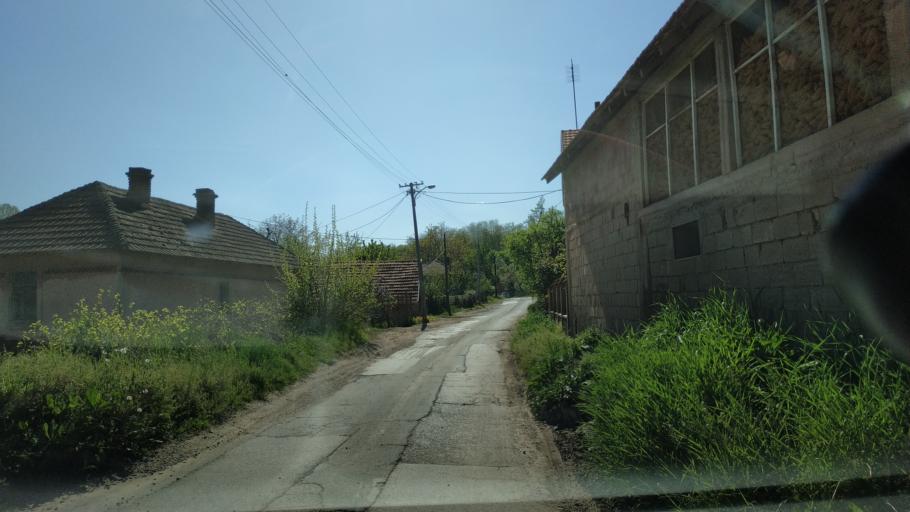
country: RS
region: Central Serbia
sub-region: Nisavski Okrug
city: Nis
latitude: 43.4152
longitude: 21.8339
